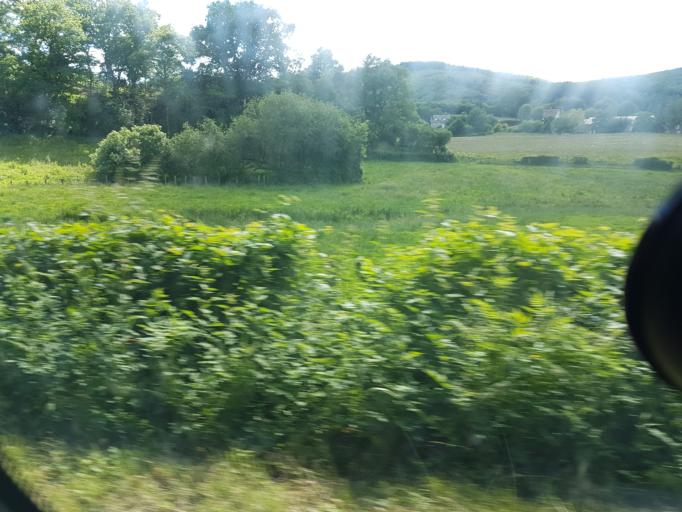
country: FR
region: Bourgogne
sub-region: Departement de la Cote-d'Or
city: Saulieu
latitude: 47.1684
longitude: 4.1560
